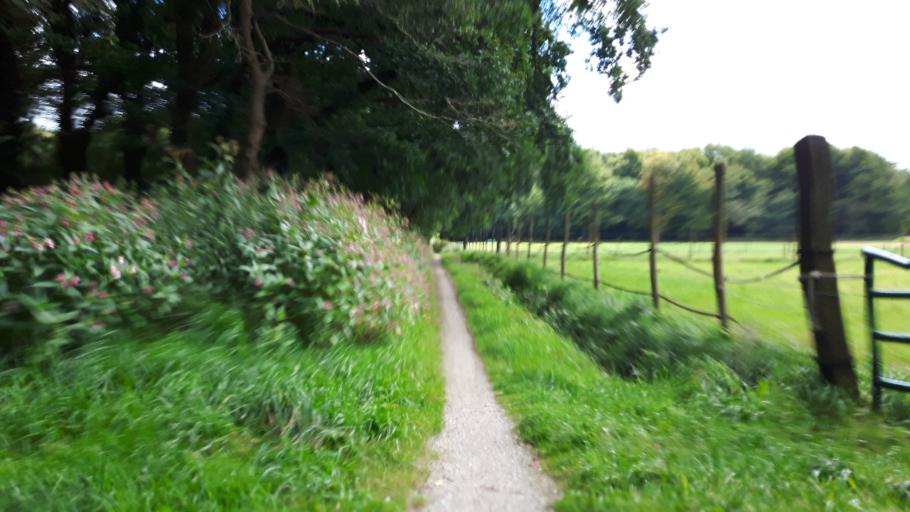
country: NL
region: Groningen
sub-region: Gemeente Haren
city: Haren
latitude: 53.1471
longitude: 6.6211
